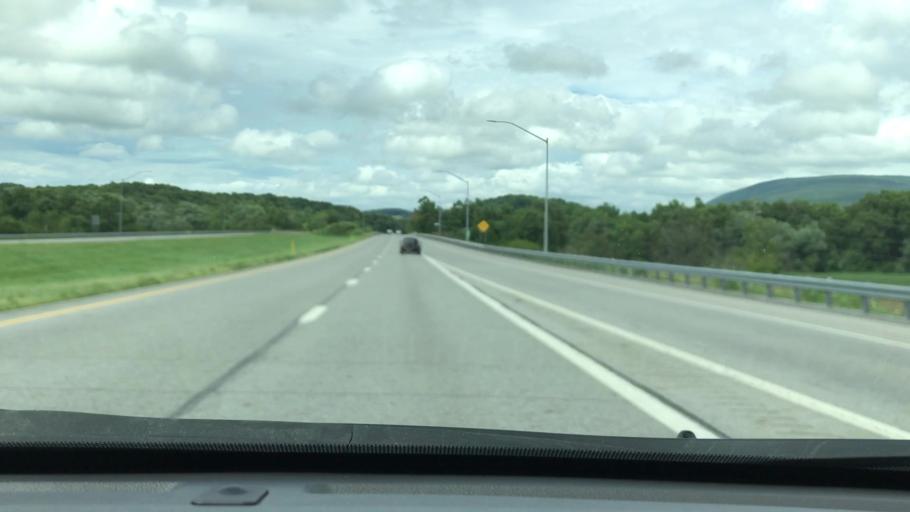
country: US
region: Pennsylvania
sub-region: Bedford County
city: Bedford
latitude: 40.0989
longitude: -78.5287
